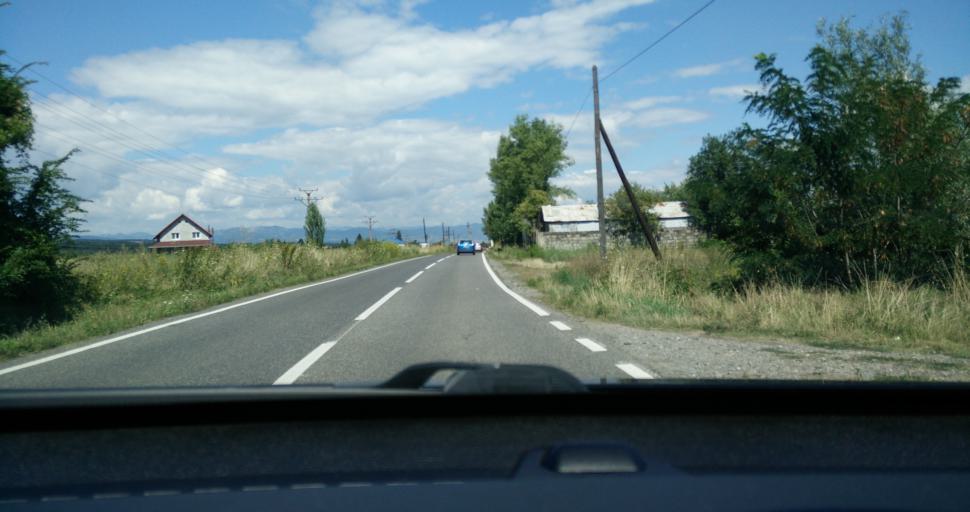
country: RO
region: Alba
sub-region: Comuna Sasciori
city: Sebesel
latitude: 45.9027
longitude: 23.5575
